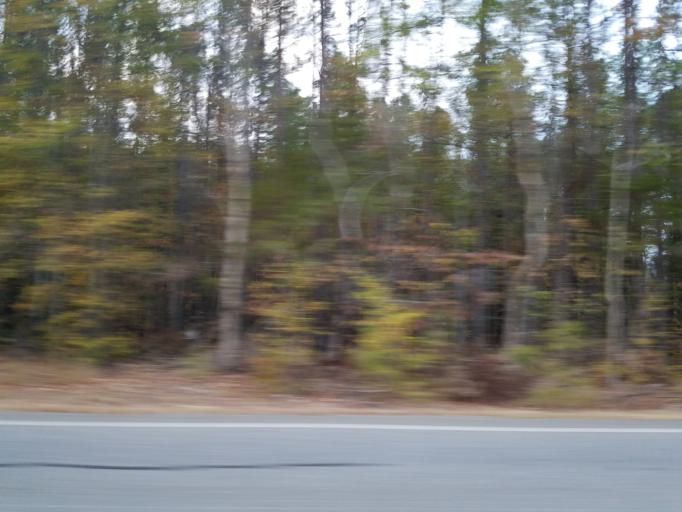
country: US
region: Georgia
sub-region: Murray County
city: Chatsworth
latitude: 34.5917
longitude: -84.6886
